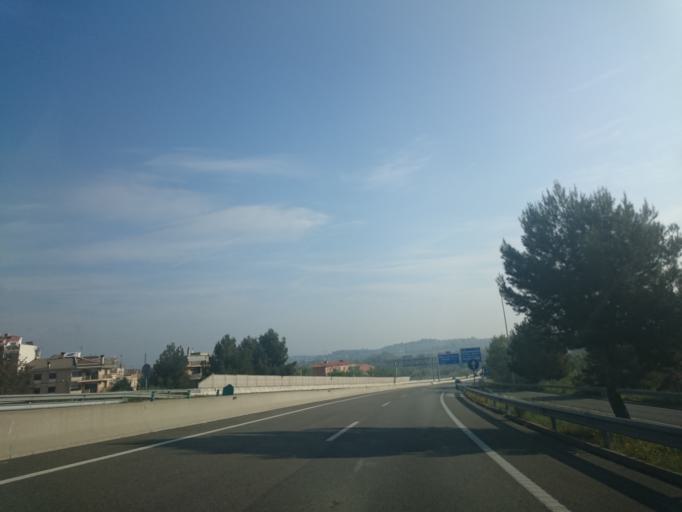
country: ES
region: Catalonia
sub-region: Provincia de Barcelona
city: Sant Joan de Vilatorrada
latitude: 41.7348
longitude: 1.8037
